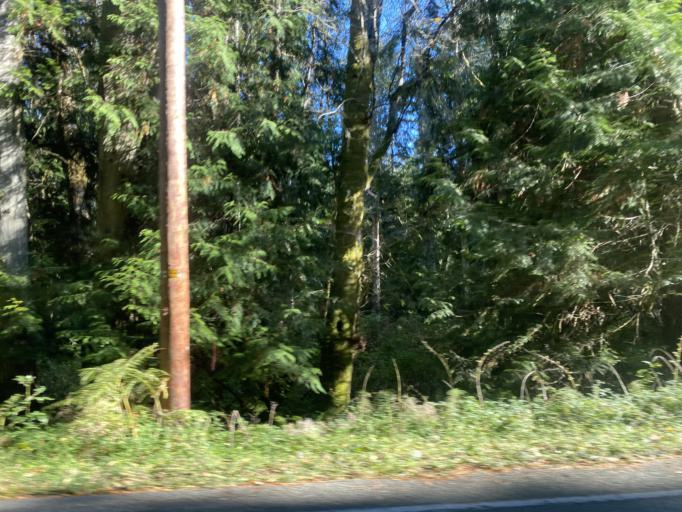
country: US
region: Washington
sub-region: Island County
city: Langley
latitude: 48.0353
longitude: -122.4212
